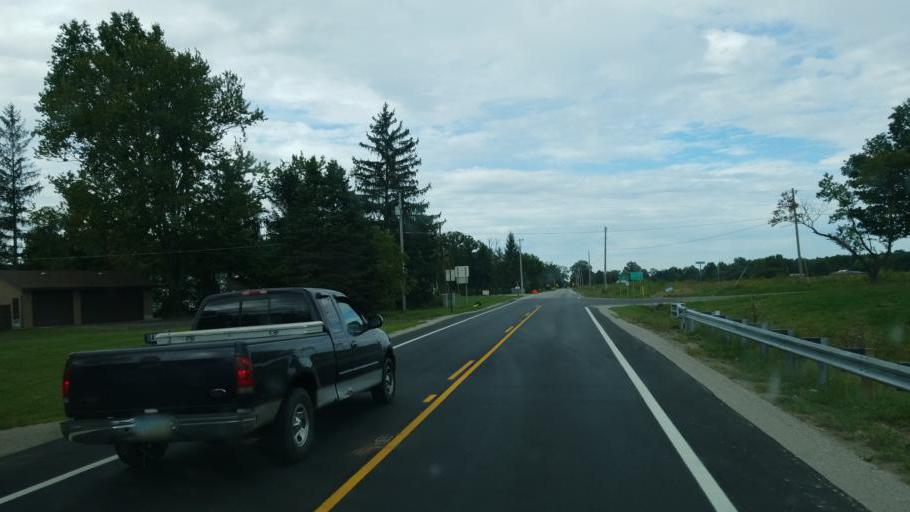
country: US
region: Ohio
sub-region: Franklin County
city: New Albany
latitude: 40.1274
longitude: -82.8100
